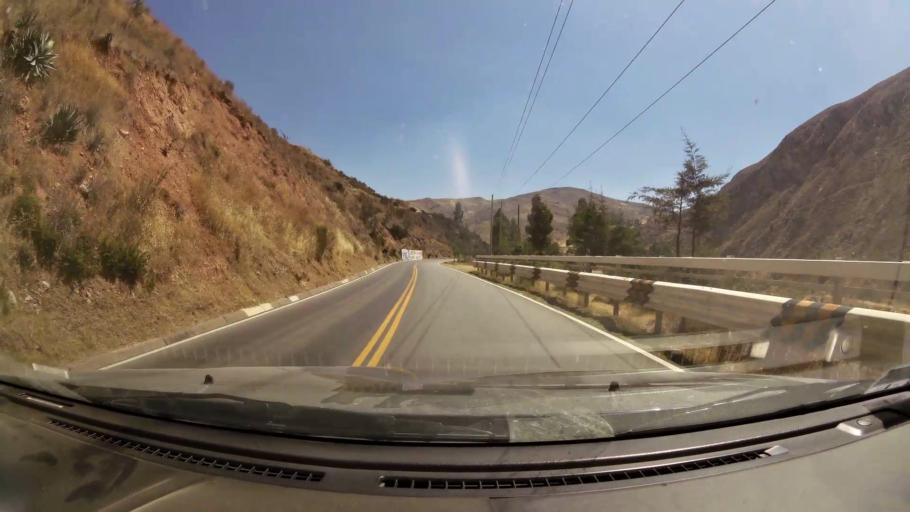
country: PE
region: Junin
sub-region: Provincia de Jauja
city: Parco
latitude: -11.7848
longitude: -75.5582
